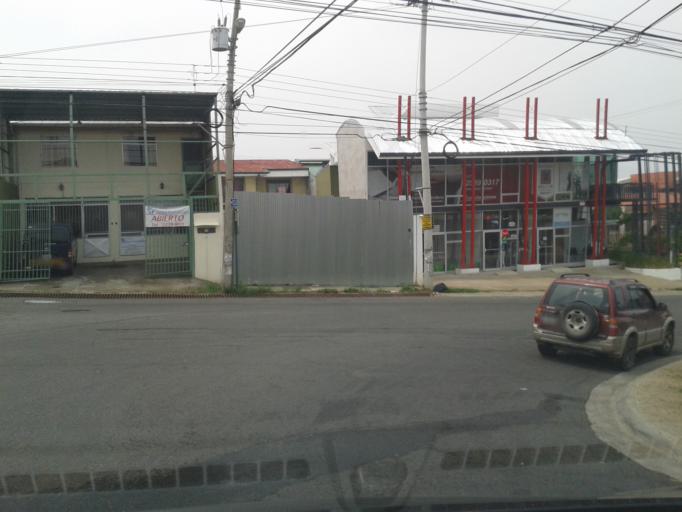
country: CR
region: Heredia
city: San Francisco
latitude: 9.9786
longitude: -84.1372
